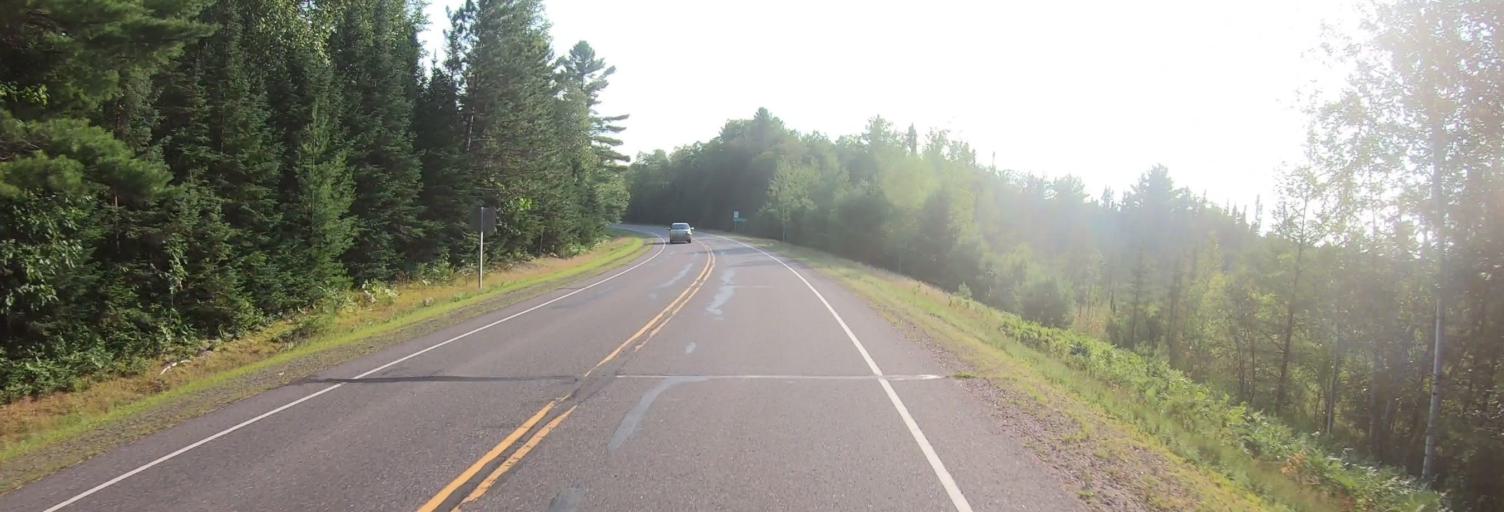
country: US
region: Wisconsin
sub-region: Ashland County
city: Ashland
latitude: 46.1648
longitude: -90.9130
